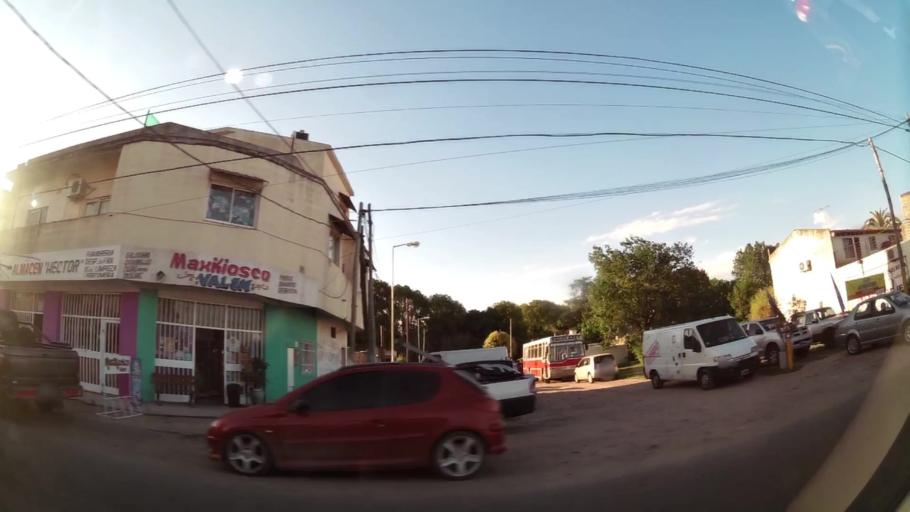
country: AR
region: Buenos Aires
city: Santa Catalina - Dique Lujan
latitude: -34.4675
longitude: -58.7531
